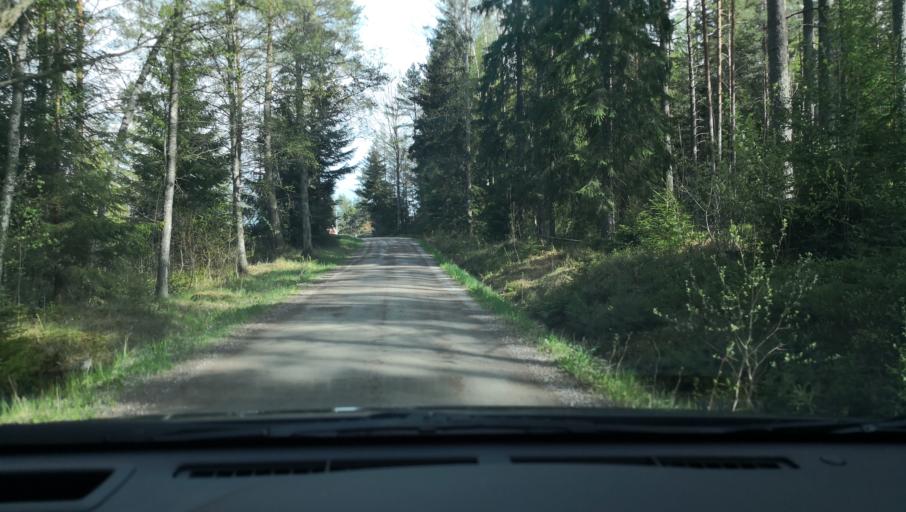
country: SE
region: OErebro
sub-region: Askersunds Kommun
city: Asbro
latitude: 59.0302
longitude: 15.0498
